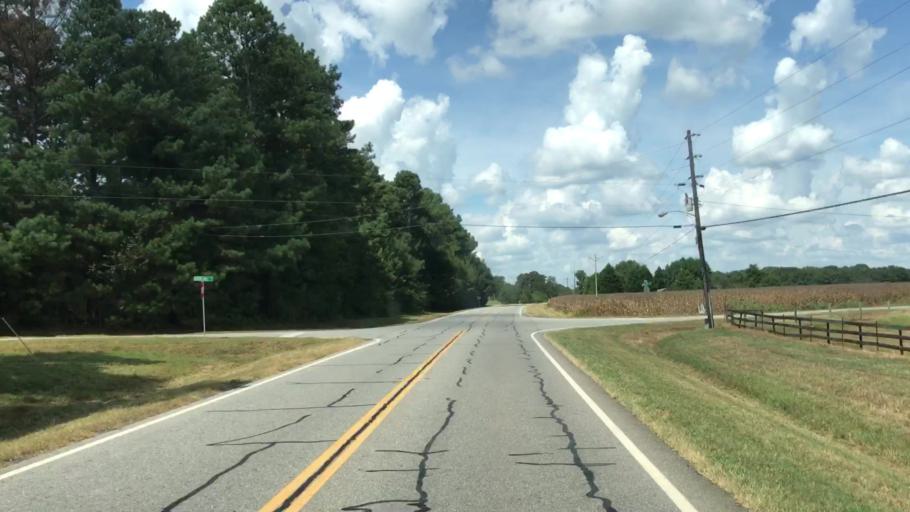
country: US
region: Georgia
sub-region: Oconee County
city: Watkinsville
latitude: 33.8132
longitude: -83.3588
